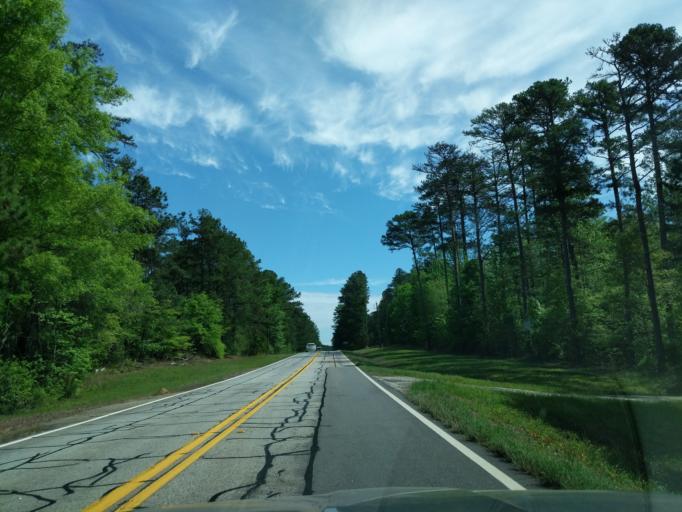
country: US
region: Georgia
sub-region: Columbia County
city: Appling
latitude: 33.6134
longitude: -82.3002
